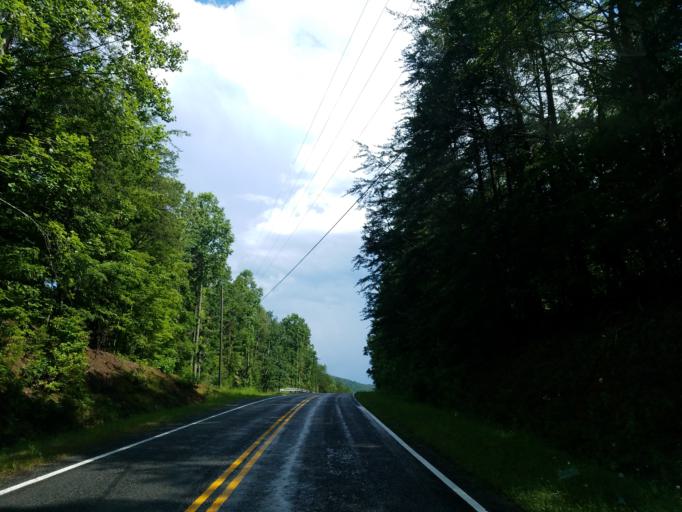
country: US
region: Georgia
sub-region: Fannin County
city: Blue Ridge
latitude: 34.6837
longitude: -84.2895
